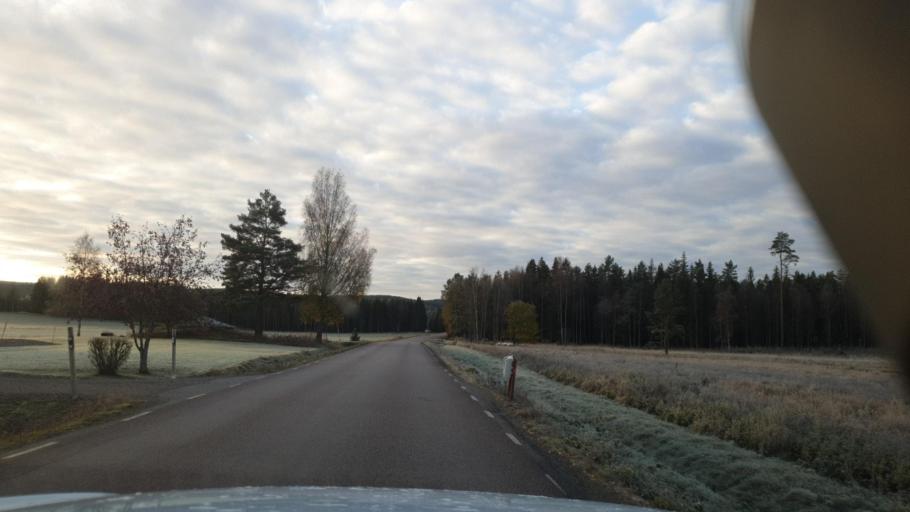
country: SE
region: Vaermland
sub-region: Eda Kommun
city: Charlottenberg
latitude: 59.7398
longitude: 12.1680
